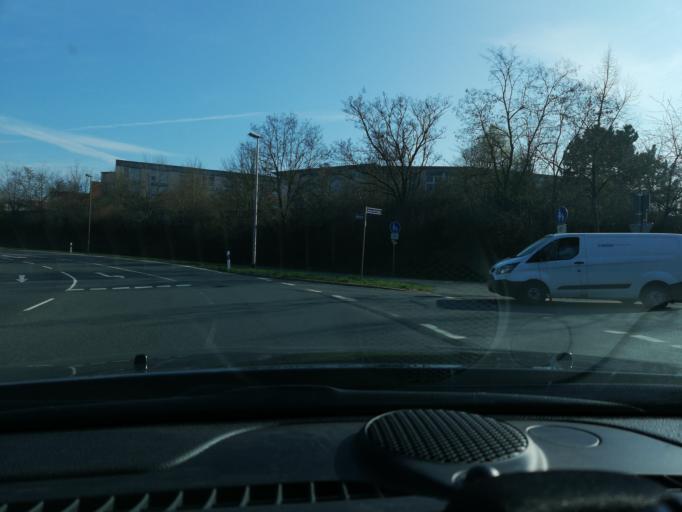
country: DE
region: Bavaria
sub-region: Regierungsbezirk Mittelfranken
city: Erlangen
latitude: 49.5954
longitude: 10.9551
